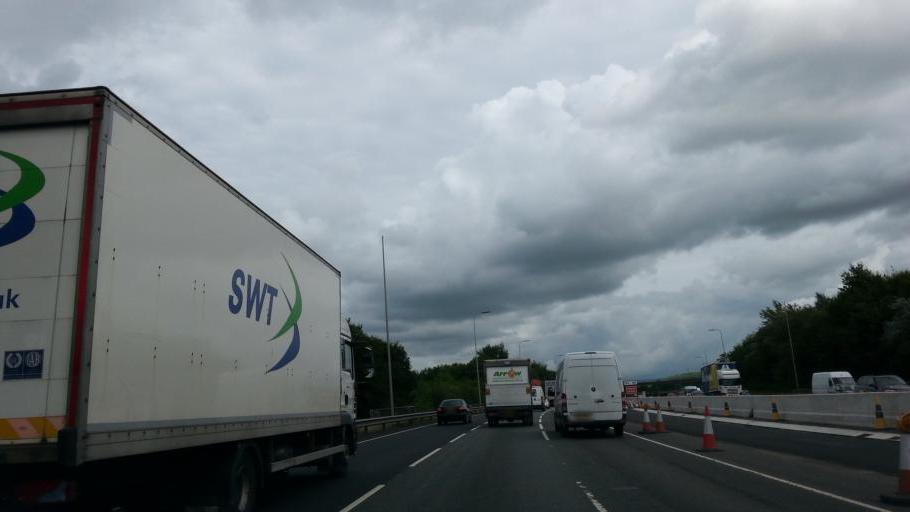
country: GB
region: England
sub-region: Borough of Rochdale
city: Rochdale
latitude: 53.5860
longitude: -2.1728
